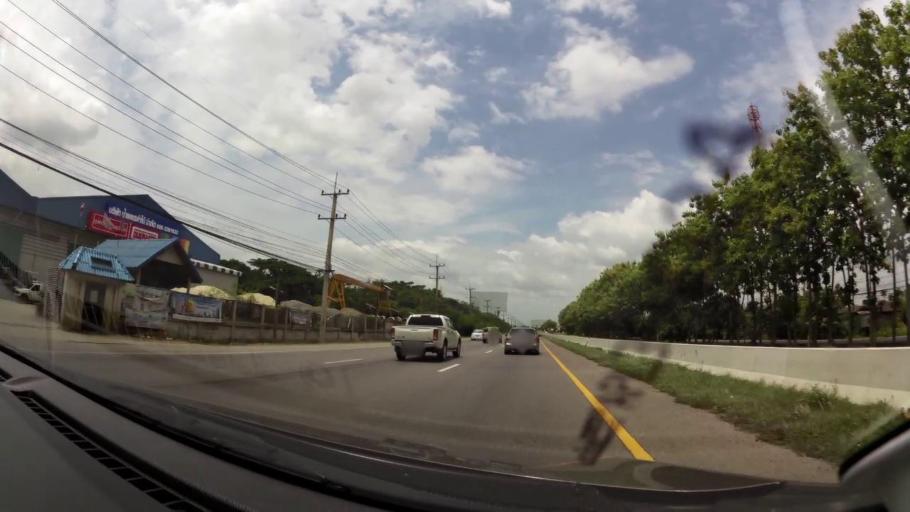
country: TH
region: Phetchaburi
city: Khao Yoi
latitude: 13.1733
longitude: 99.8390
